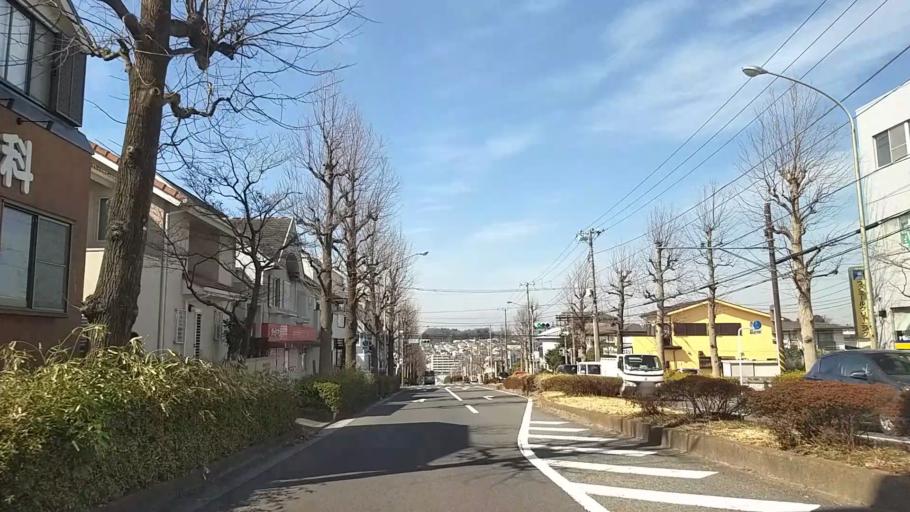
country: JP
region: Kanagawa
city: Kamakura
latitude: 35.3776
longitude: 139.5613
